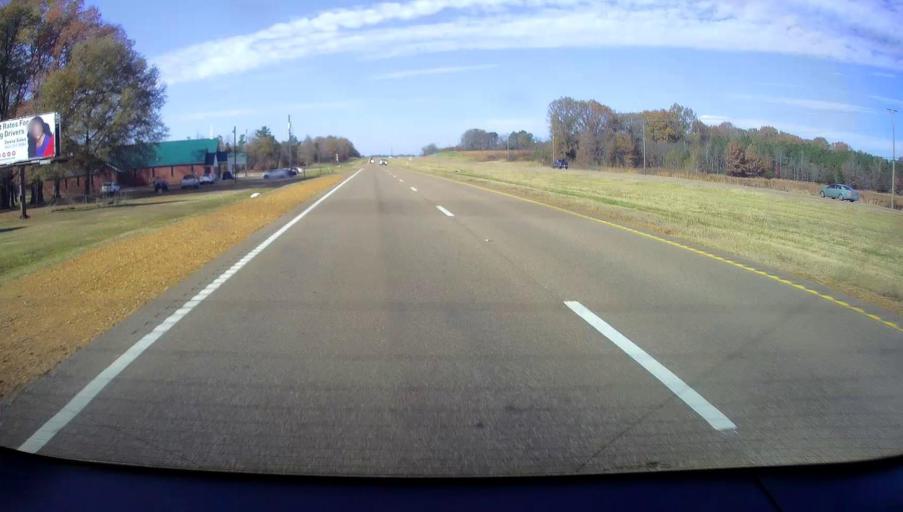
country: US
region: Tennessee
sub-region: Fayette County
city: Piperton
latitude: 34.9800
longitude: -89.5807
